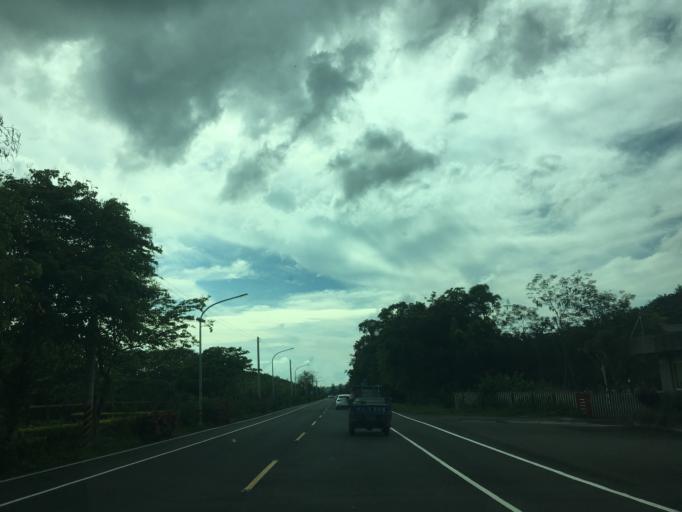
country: TW
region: Taiwan
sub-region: Chiayi
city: Jiayi Shi
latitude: 23.4442
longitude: 120.5899
